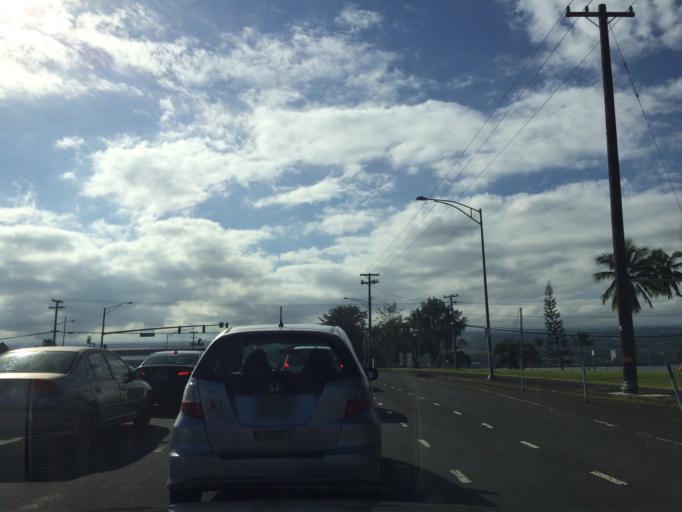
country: US
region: Hawaii
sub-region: Hawaii County
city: Hilo
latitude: 19.7227
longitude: -155.0689
